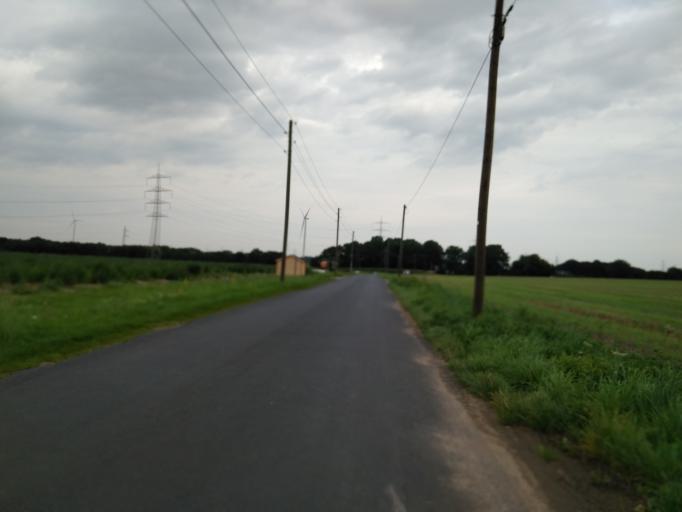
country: DE
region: North Rhine-Westphalia
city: Dorsten
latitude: 51.6176
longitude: 6.9448
